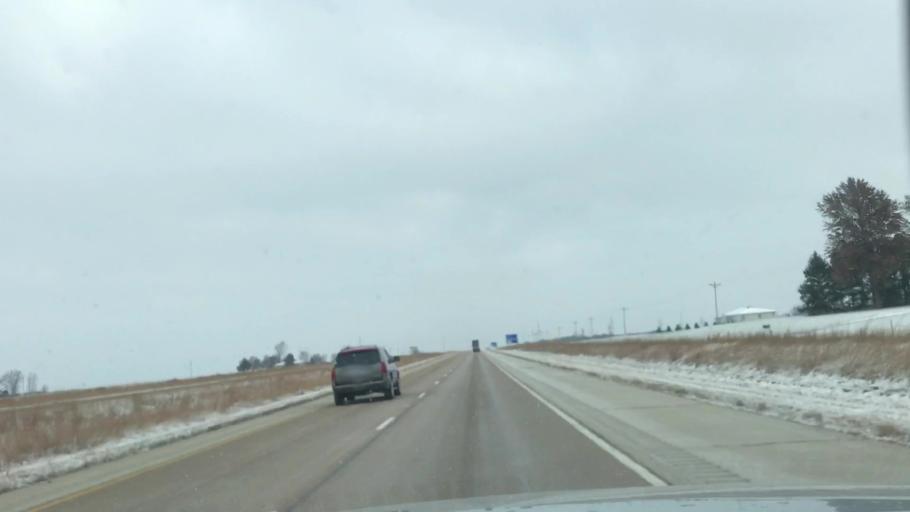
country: US
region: Illinois
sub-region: Montgomery County
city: Litchfield
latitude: 39.2508
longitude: -89.6412
